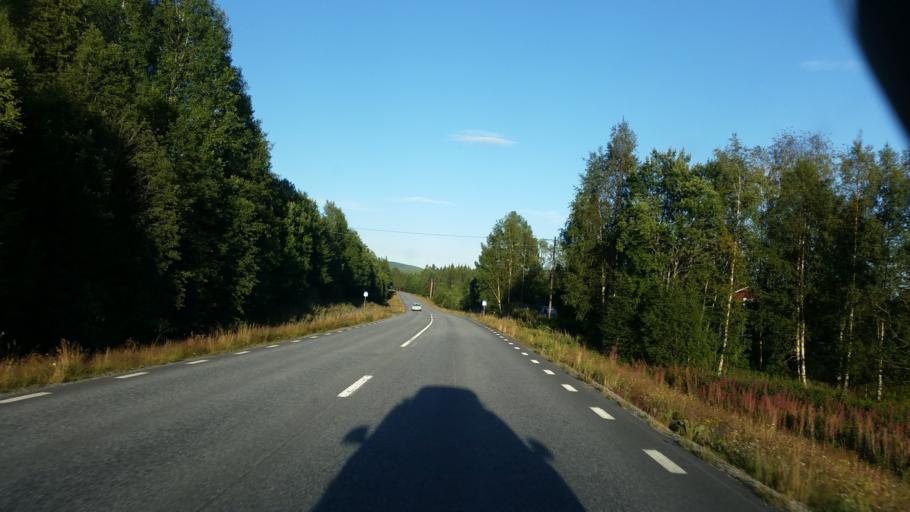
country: SE
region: Vaesterbotten
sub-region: Dorotea Kommun
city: Dorotea
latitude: 64.2546
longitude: 16.4570
